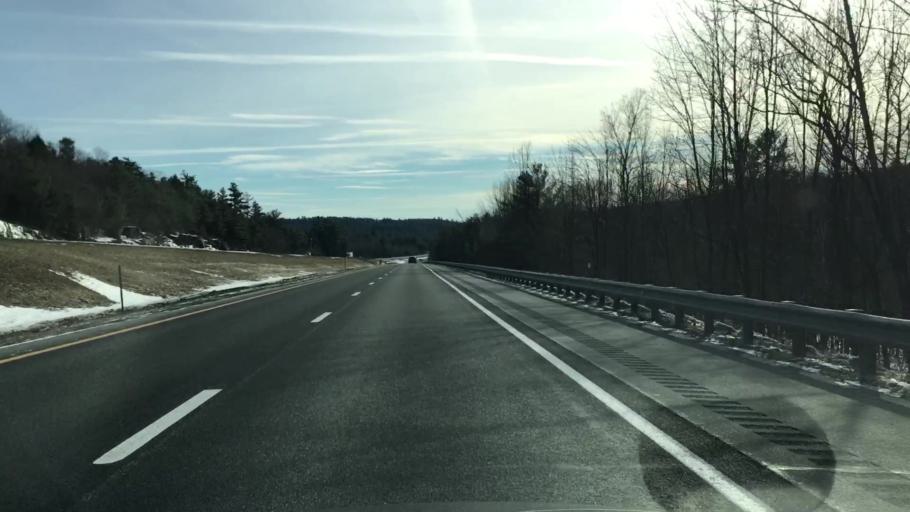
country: US
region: New Hampshire
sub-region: Sullivan County
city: Grantham
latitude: 43.5473
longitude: -72.1399
